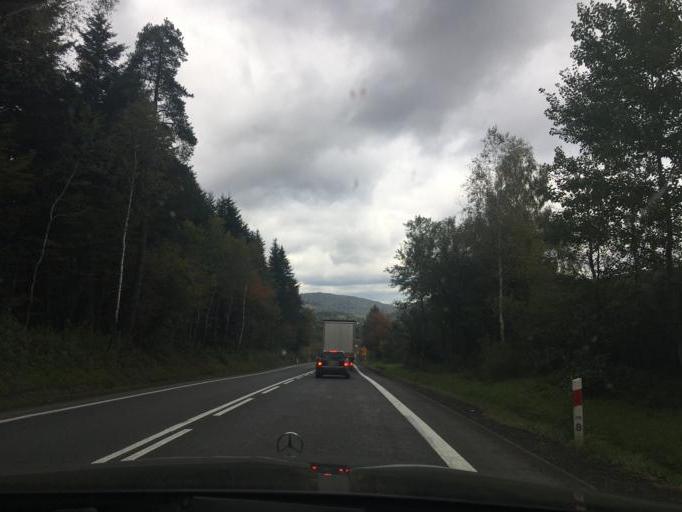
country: PL
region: Subcarpathian Voivodeship
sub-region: Powiat krosnienski
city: Dukla
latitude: 49.4908
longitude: 21.7041
